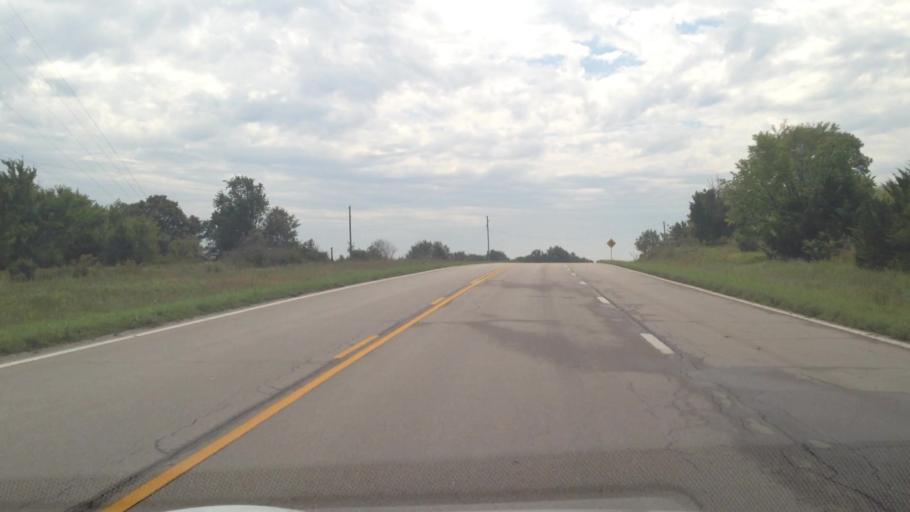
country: US
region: Kansas
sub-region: Bourbon County
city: Fort Scott
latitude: 37.8280
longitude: -94.9794
